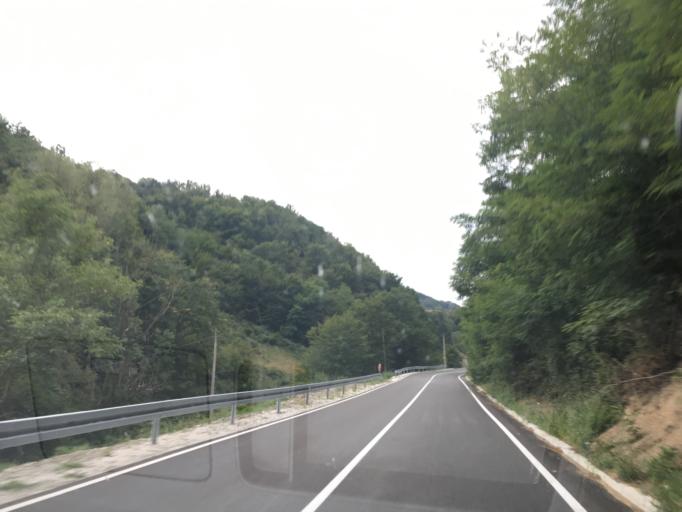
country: RS
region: Central Serbia
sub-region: Moravicki Okrug
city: Gornji Milanovac
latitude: 44.1578
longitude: 20.5079
